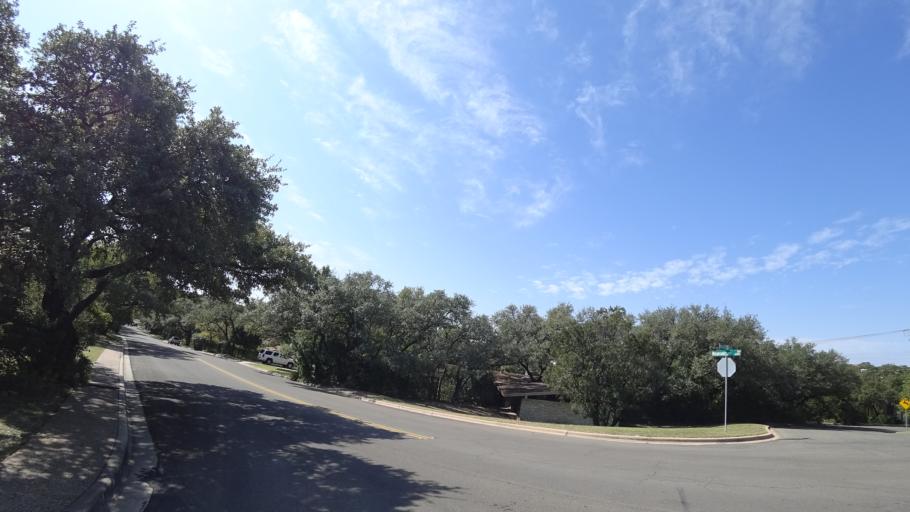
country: US
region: Texas
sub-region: Travis County
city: West Lake Hills
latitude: 30.3489
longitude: -97.7638
